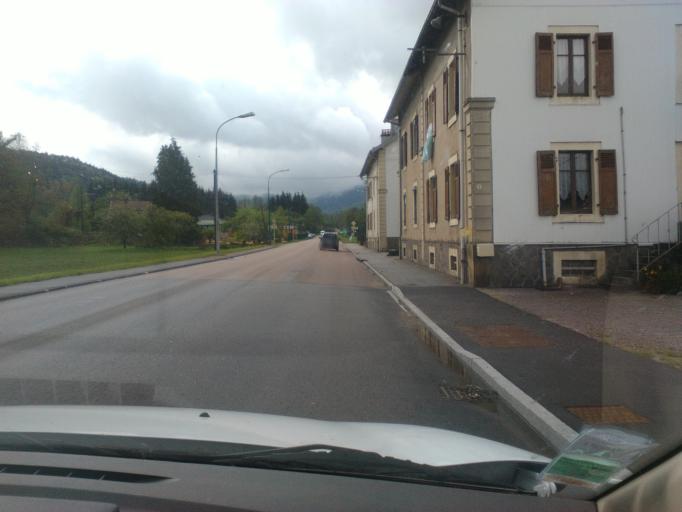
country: FR
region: Lorraine
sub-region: Departement des Vosges
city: Vagney
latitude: 47.9904
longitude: 6.7200
